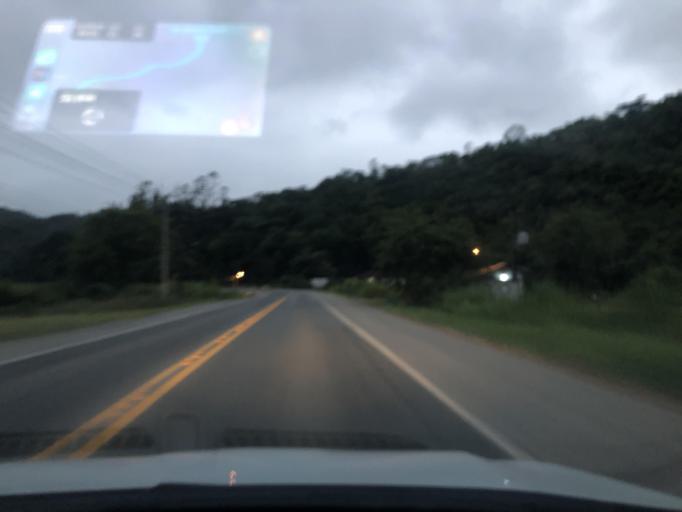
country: BR
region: Santa Catarina
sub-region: Jaragua Do Sul
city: Jaragua do Sul
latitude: -26.6483
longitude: -49.0188
